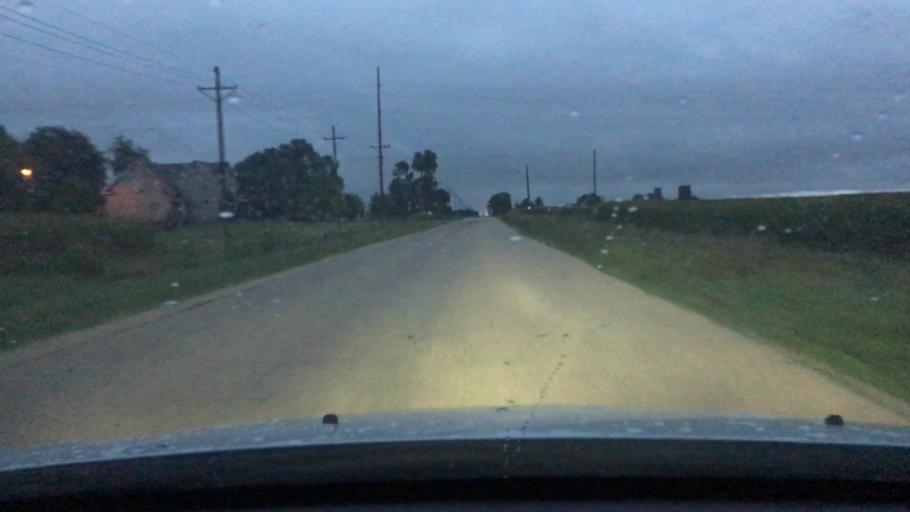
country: US
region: Illinois
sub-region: Ogle County
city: Rochelle
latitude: 41.8985
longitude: -89.0016
